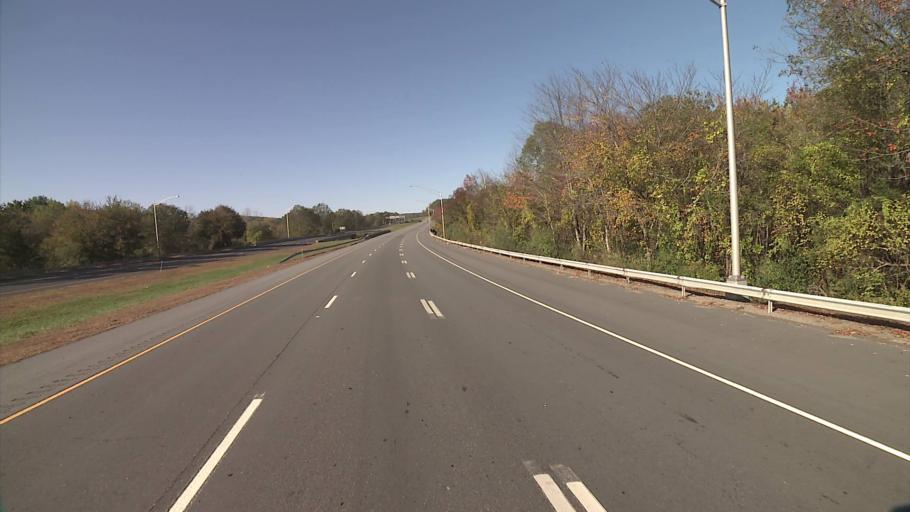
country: US
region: Connecticut
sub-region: Windham County
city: Willimantic
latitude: 41.7243
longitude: -72.2498
